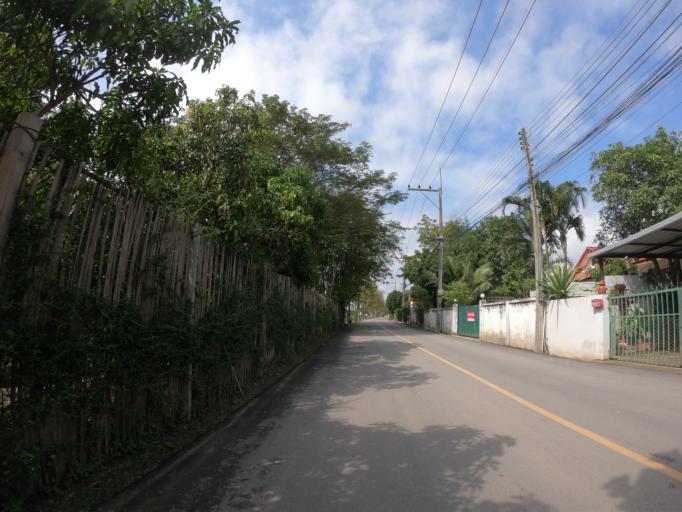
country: TH
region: Chiang Mai
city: San Sai
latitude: 18.8628
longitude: 99.0253
